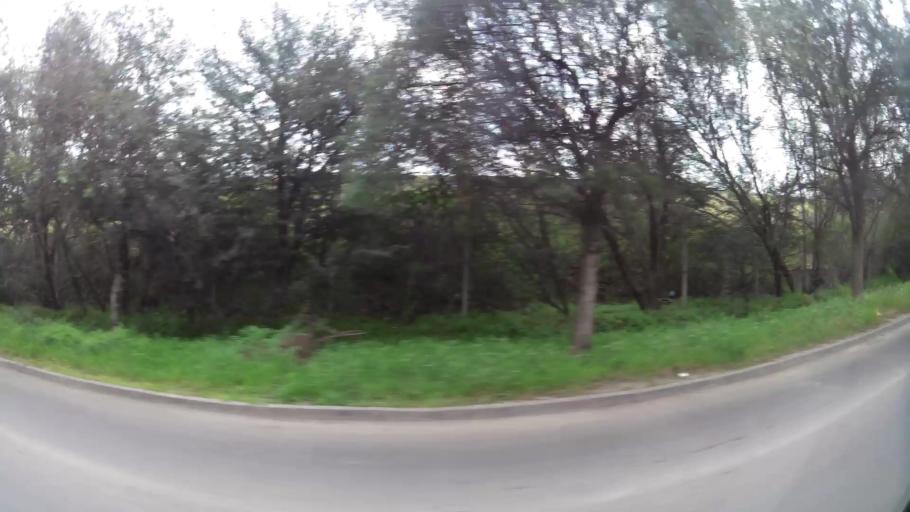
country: CL
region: Santiago Metropolitan
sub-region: Provincia de Chacabuco
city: Chicureo Abajo
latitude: -33.2064
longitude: -70.6661
